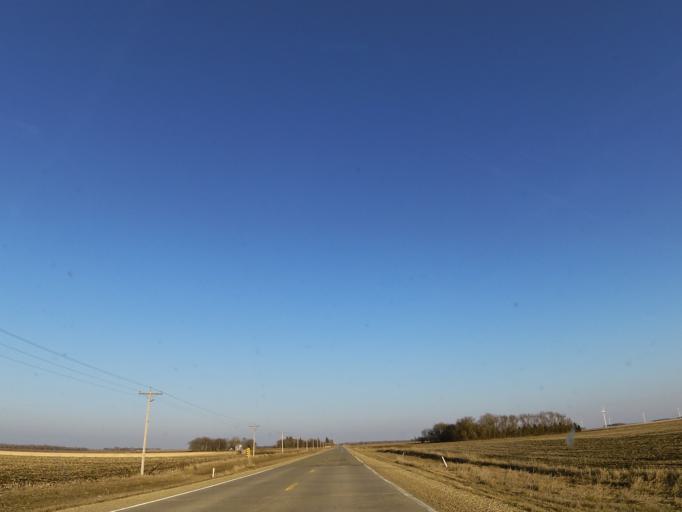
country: US
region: Iowa
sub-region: Worth County
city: Northwood
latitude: 43.4368
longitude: -93.0970
